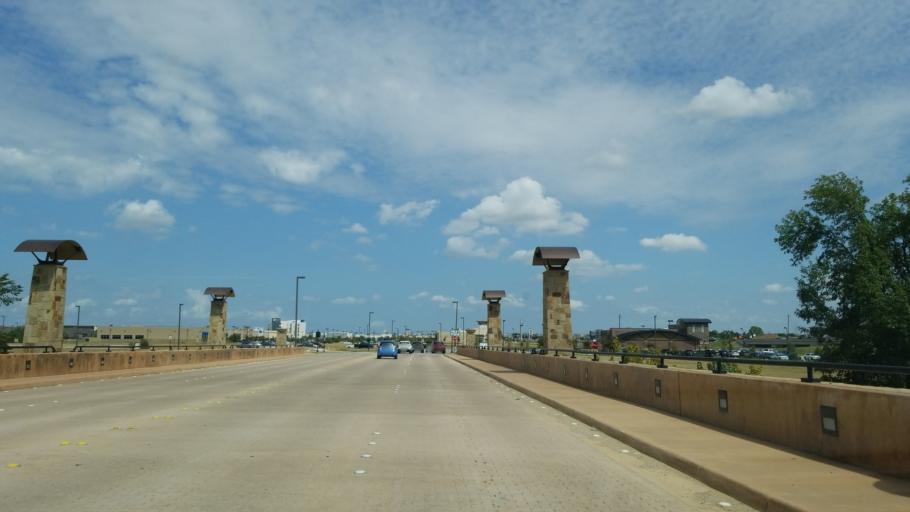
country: US
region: Texas
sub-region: Tarrant County
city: Euless
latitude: 32.8672
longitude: -97.1036
